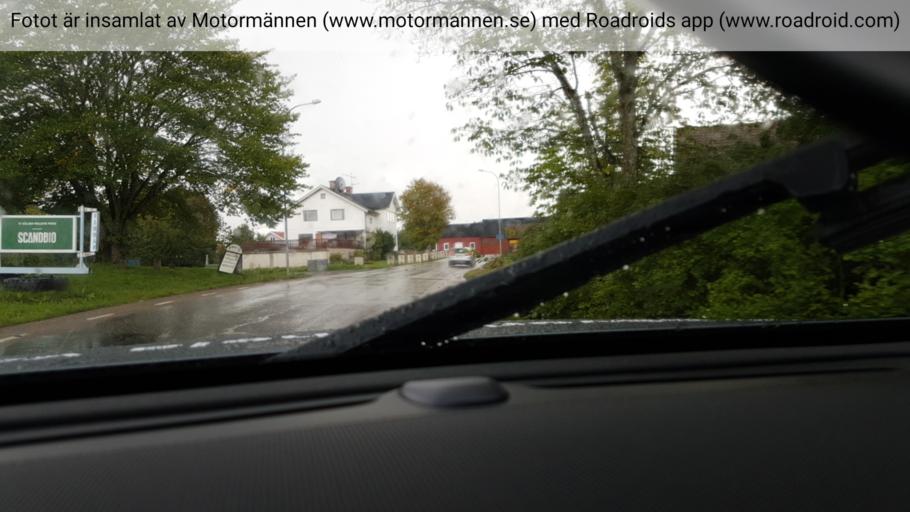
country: SE
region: Vaestra Goetaland
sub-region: Vanersborgs Kommun
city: Vanersborg
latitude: 58.3635
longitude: 12.2728
